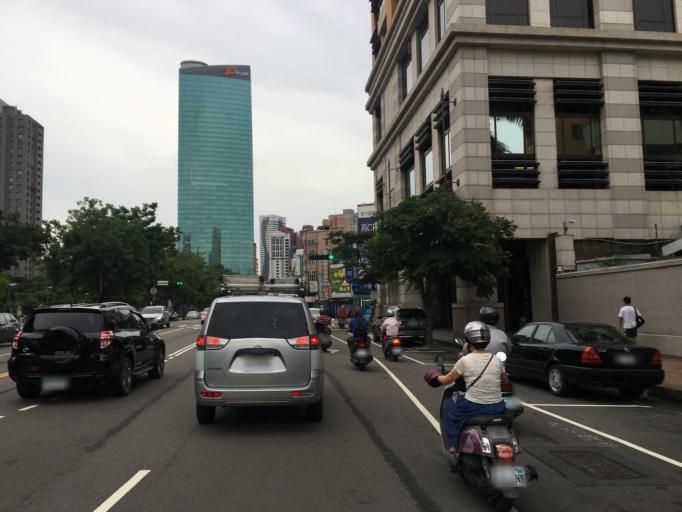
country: TW
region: Taiwan
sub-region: Taichung City
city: Taichung
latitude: 24.1461
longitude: 120.6654
